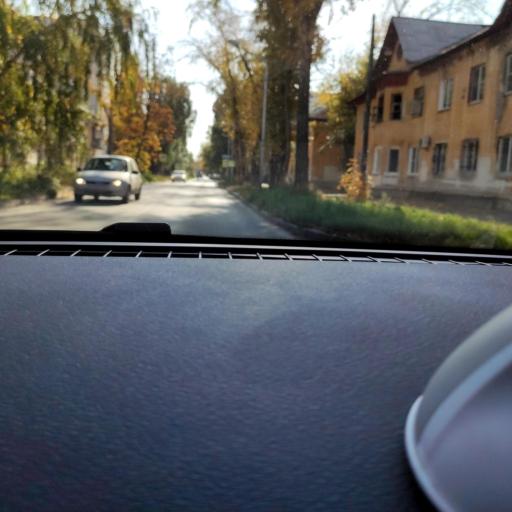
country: RU
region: Samara
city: Samara
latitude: 53.2266
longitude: 50.2670
